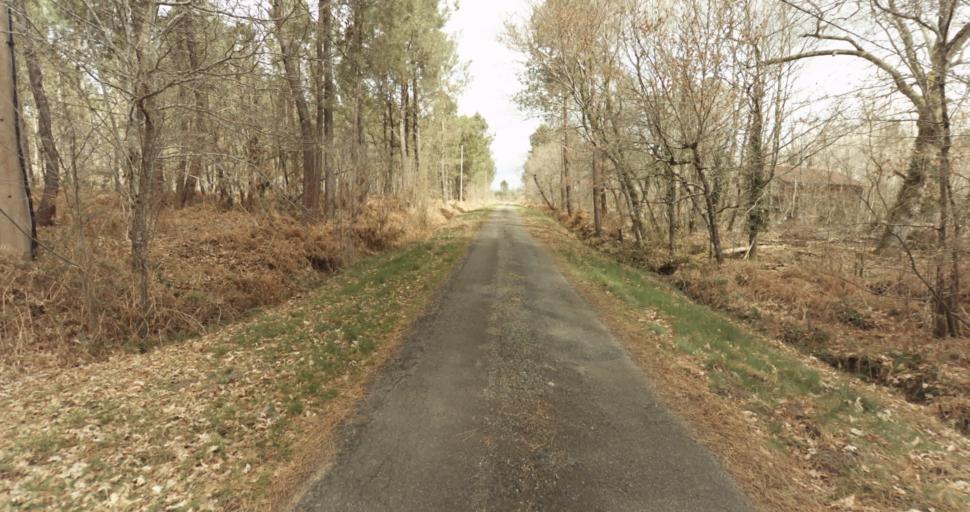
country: FR
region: Aquitaine
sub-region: Departement des Landes
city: Roquefort
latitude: 44.0814
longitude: -0.3928
